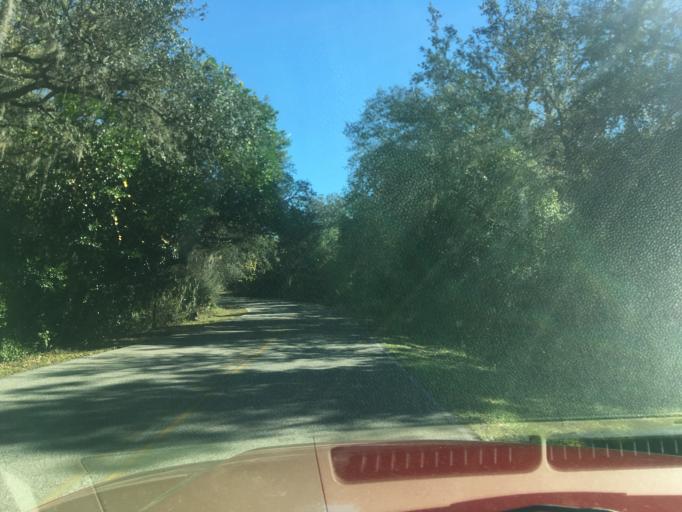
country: US
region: Florida
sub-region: Hillsborough County
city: Thonotosassa
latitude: 28.0759
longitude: -82.3495
